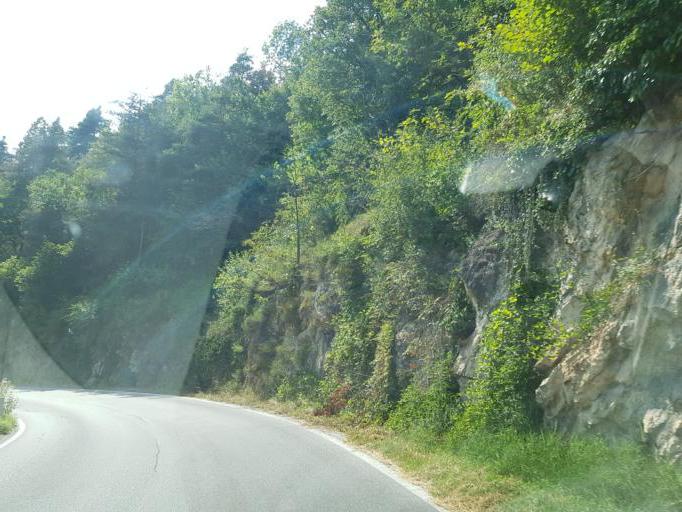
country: IT
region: Piedmont
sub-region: Provincia di Cuneo
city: San Damiano Macra
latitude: 44.4934
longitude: 7.2364
